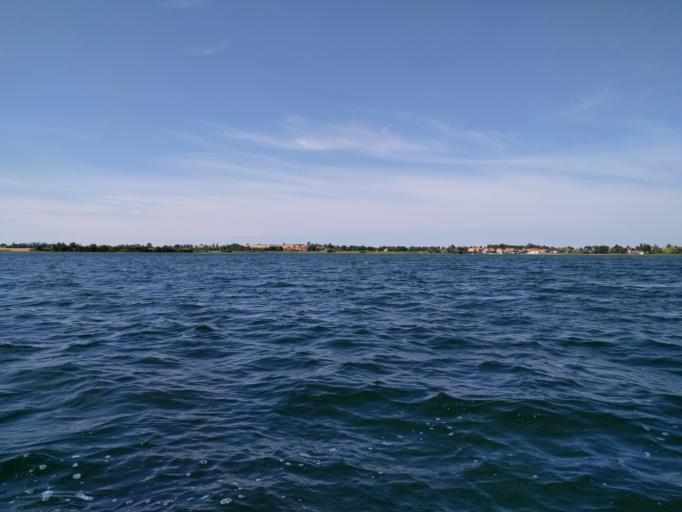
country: DK
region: South Denmark
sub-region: Kerteminde Kommune
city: Kerteminde
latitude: 55.4426
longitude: 10.6423
